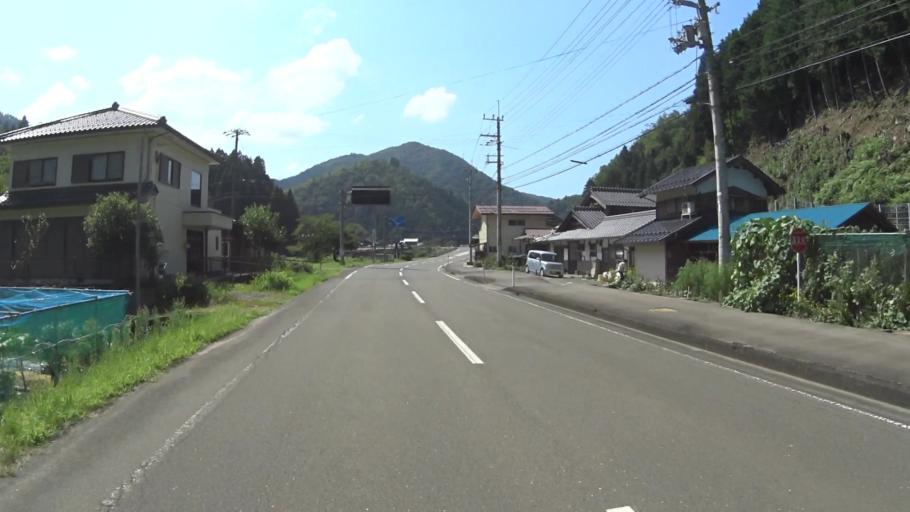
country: JP
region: Fukui
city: Obama
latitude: 35.3986
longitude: 135.6146
